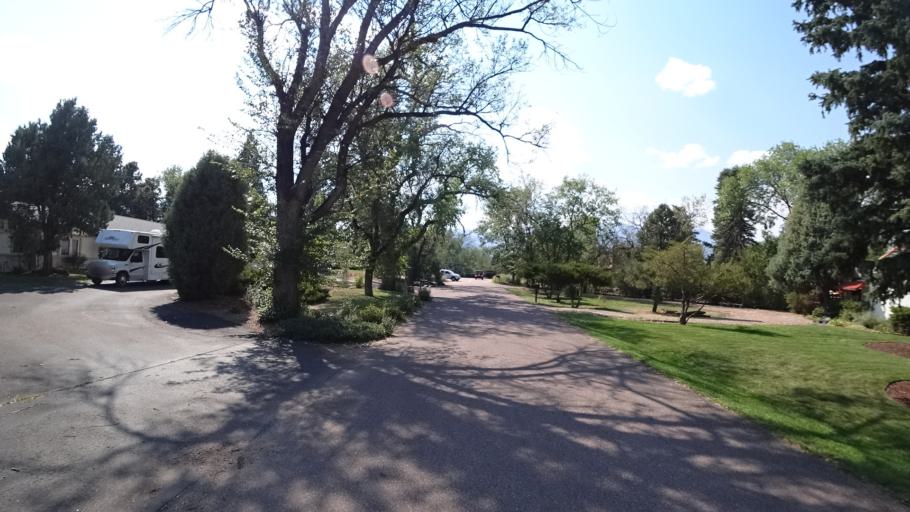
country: US
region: Colorado
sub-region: El Paso County
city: Colorado Springs
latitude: 38.7990
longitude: -104.8344
